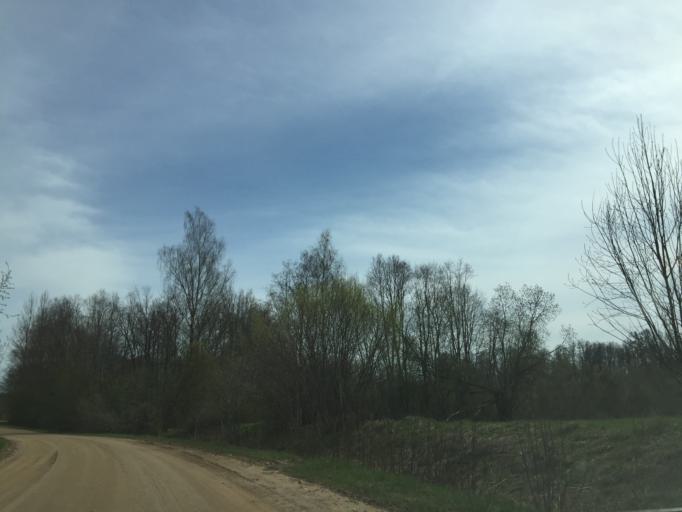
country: LV
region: Ludzas Rajons
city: Ludza
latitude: 56.5289
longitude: 27.5439
